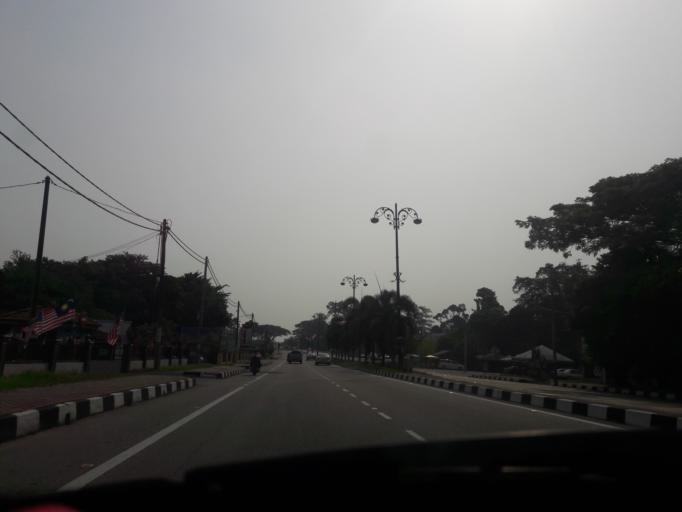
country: MY
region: Kedah
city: Kulim
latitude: 5.3632
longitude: 100.5495
